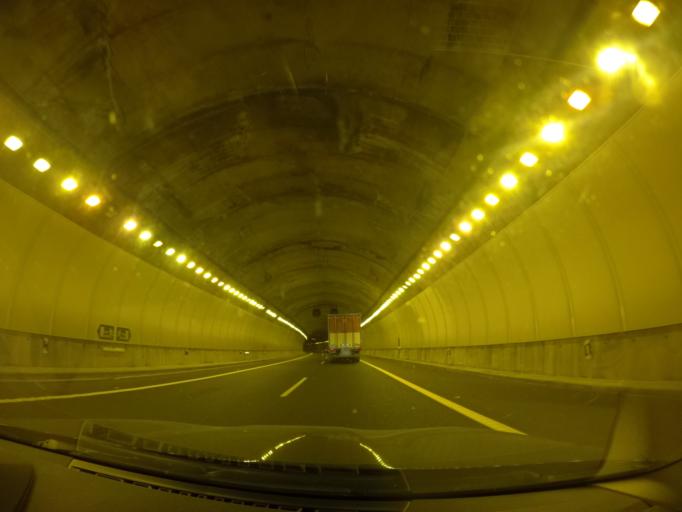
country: ES
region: Andalusia
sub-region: Provincia de Malaga
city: Nerja
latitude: 36.7664
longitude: -3.8636
